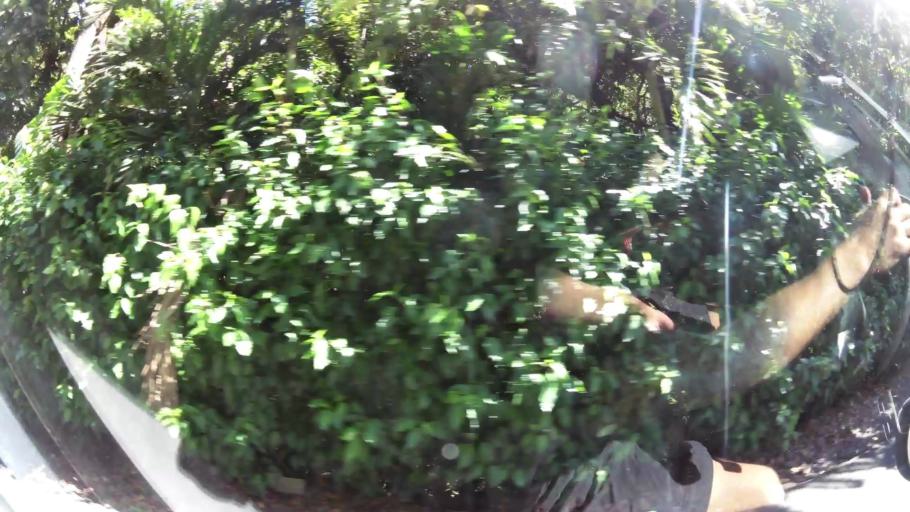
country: CR
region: Puntarenas
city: Quepos
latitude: 9.4041
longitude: -84.1598
